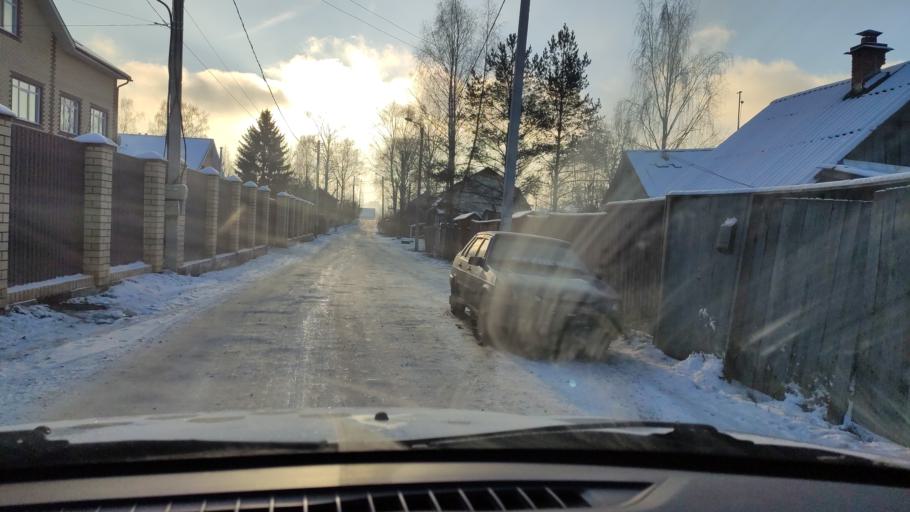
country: RU
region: Perm
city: Perm
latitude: 58.0315
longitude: 56.2286
